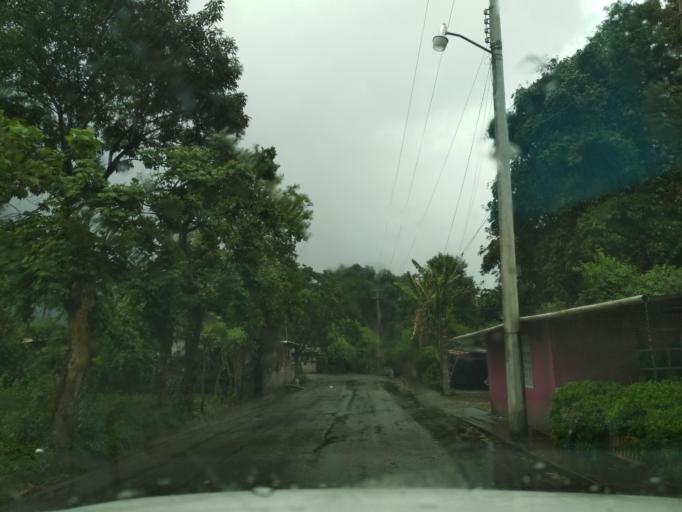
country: MX
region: Veracruz
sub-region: Mariano Escobedo
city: Chicola
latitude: 18.9018
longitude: -97.1170
